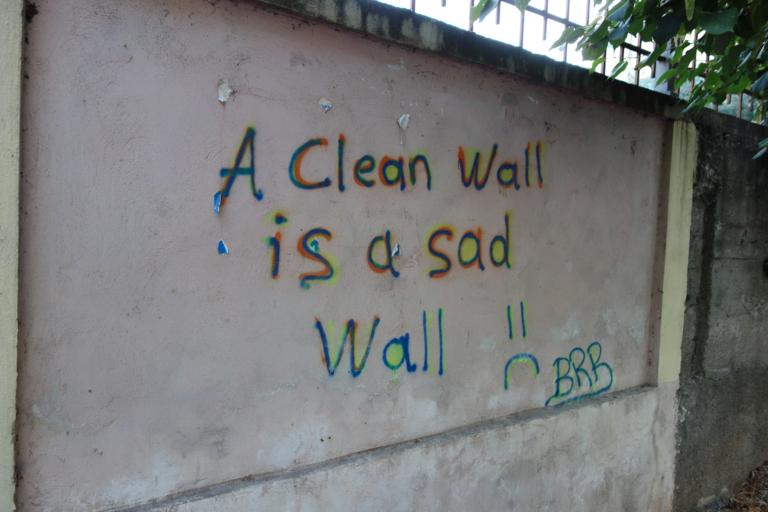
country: AL
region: Tirane
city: Tirana
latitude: 41.3224
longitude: 19.8068
